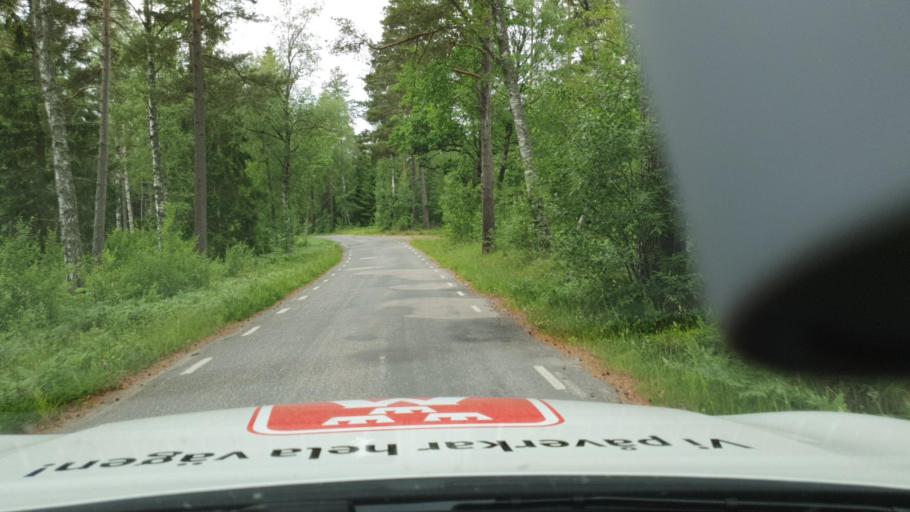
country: SE
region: Vaestra Goetaland
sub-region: Tidaholms Kommun
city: Tidaholm
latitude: 58.1656
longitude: 14.0245
